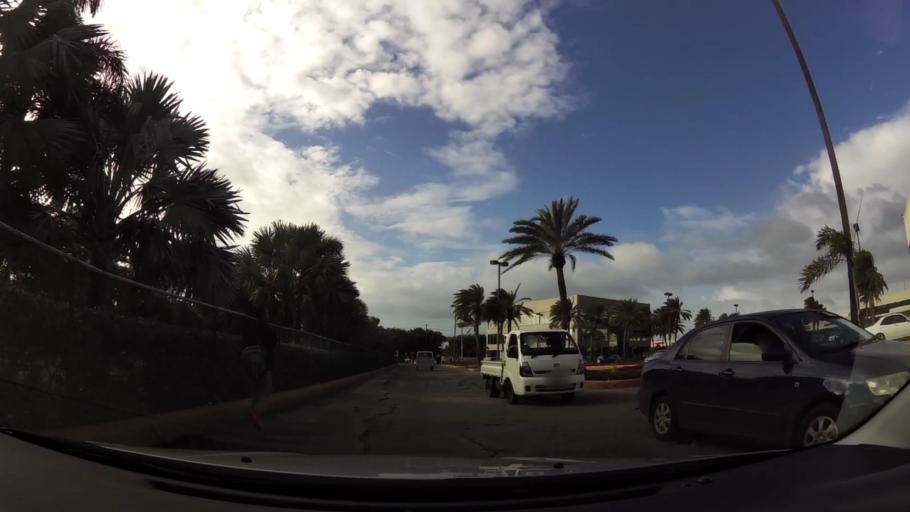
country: AG
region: Saint John
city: Saint John's
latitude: 17.1297
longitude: -61.8356
